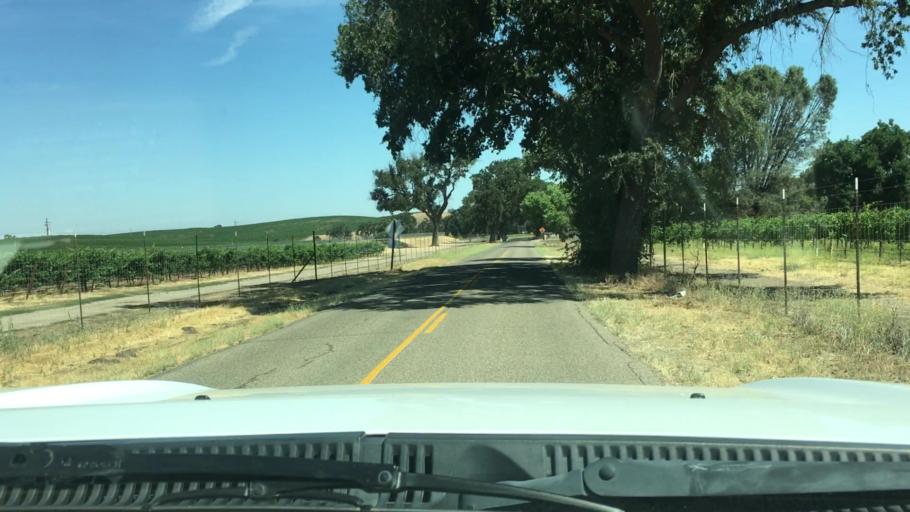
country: US
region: California
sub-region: San Luis Obispo County
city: Paso Robles
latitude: 35.5705
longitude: -120.6075
